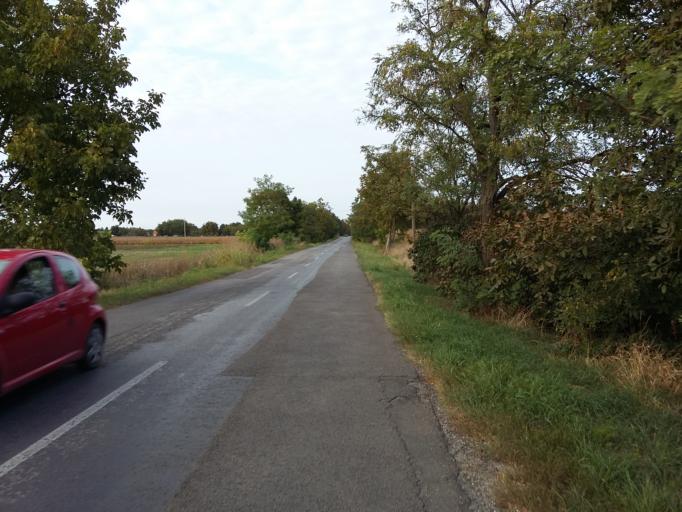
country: HU
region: Csongrad
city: Szeged
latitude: 46.2152
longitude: 20.1096
